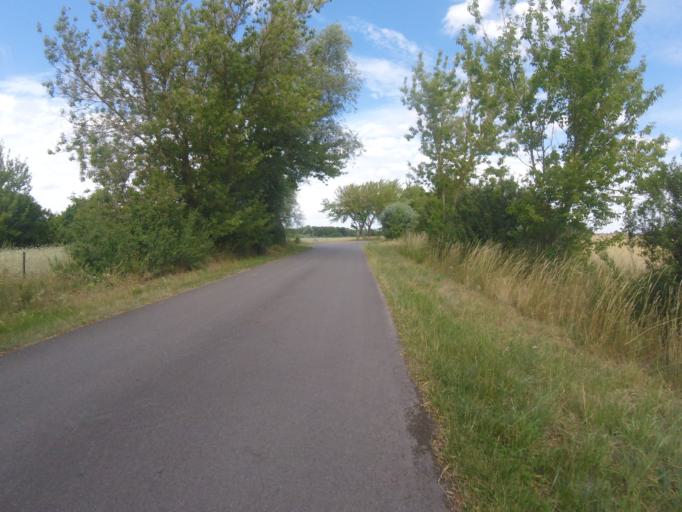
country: DE
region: Brandenburg
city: Bestensee
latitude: 52.2312
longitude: 13.7049
